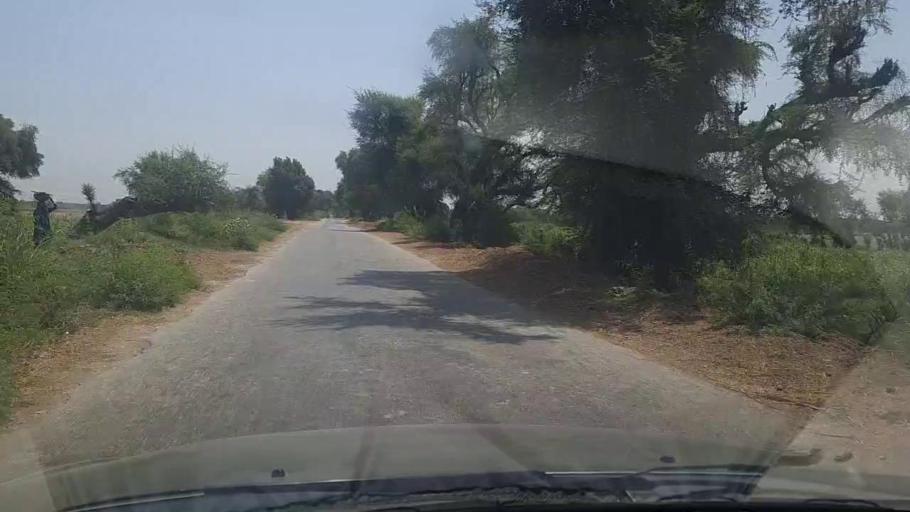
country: PK
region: Sindh
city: Tando Jam
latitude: 25.2816
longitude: 68.6061
